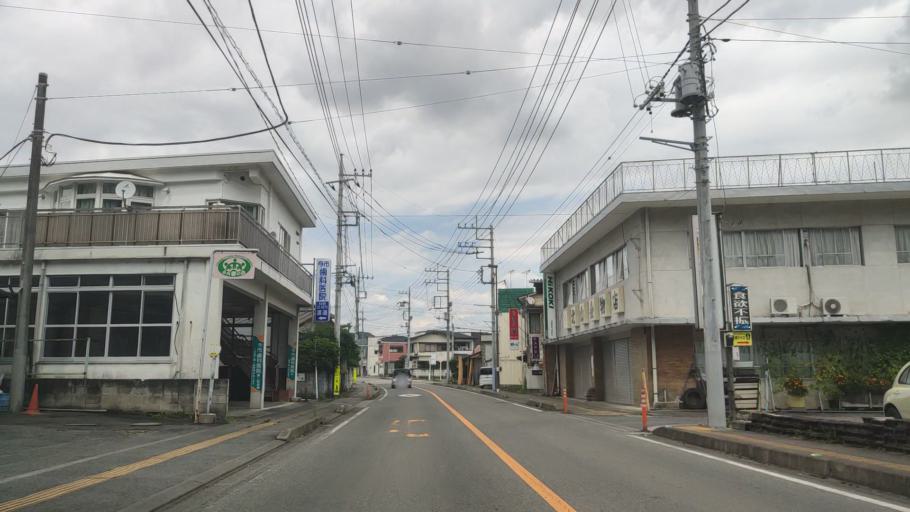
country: JP
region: Tochigi
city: Imaichi
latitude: 36.7228
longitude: 139.6932
